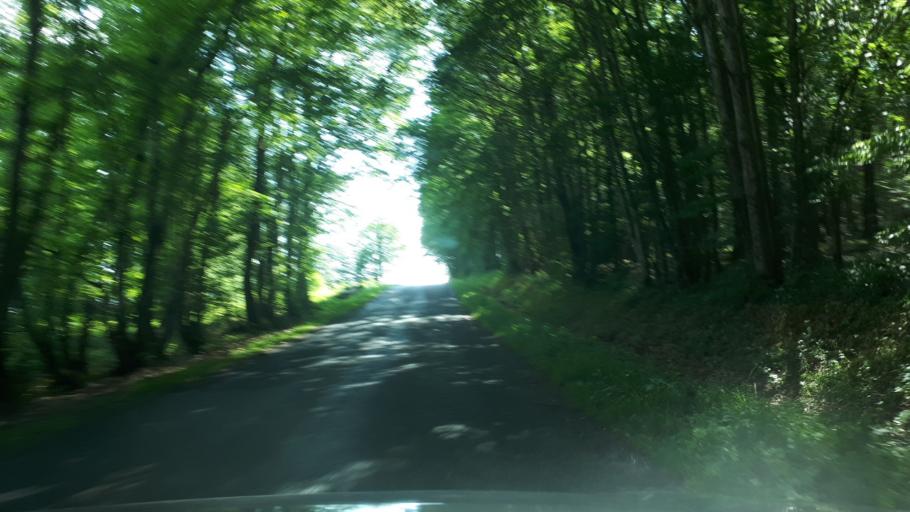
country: FR
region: Centre
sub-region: Departement du Cher
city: Henrichemont
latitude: 47.4040
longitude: 2.6006
